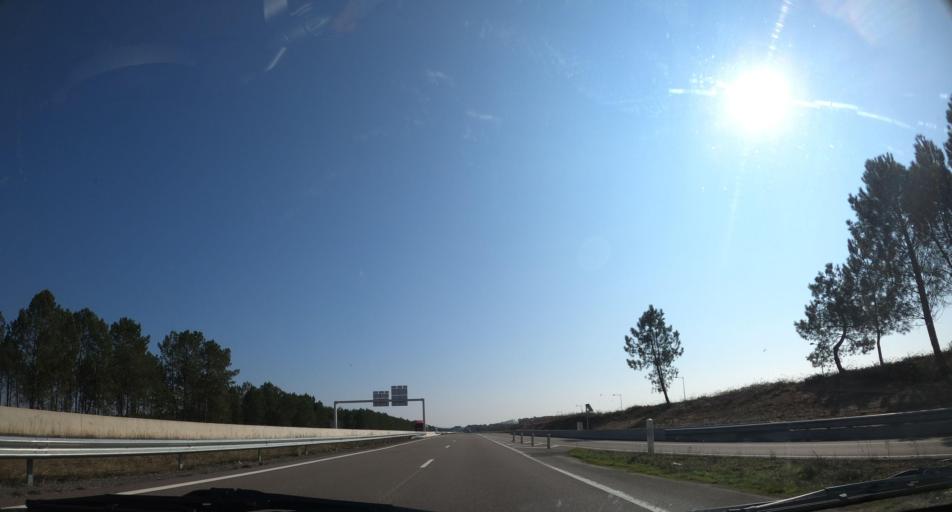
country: FR
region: Aquitaine
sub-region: Departement des Landes
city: Saint-Geours-de-Maremne
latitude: 43.6966
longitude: -1.2248
